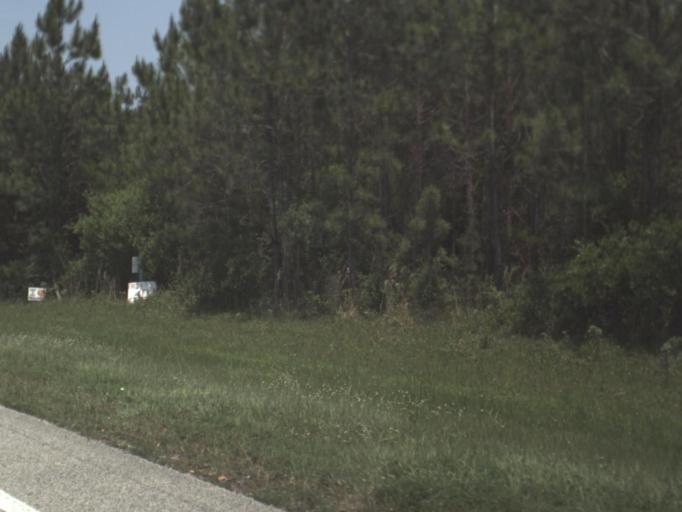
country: US
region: Florida
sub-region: Duval County
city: Baldwin
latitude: 30.1835
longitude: -82.0215
